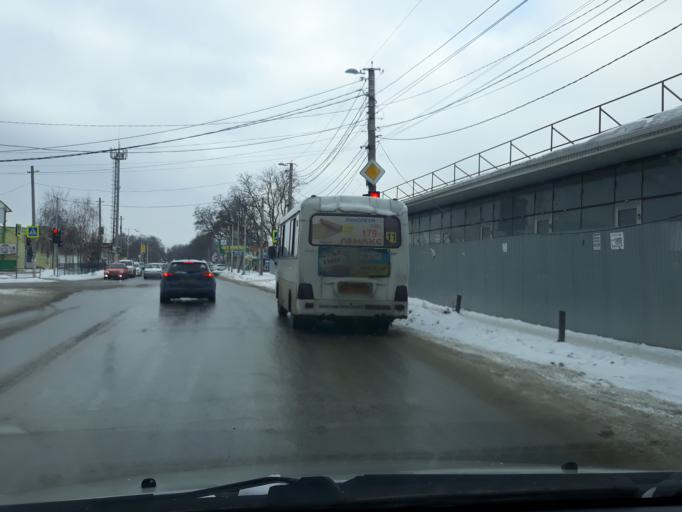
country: RU
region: Rostov
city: Taganrog
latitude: 47.2603
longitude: 38.9125
